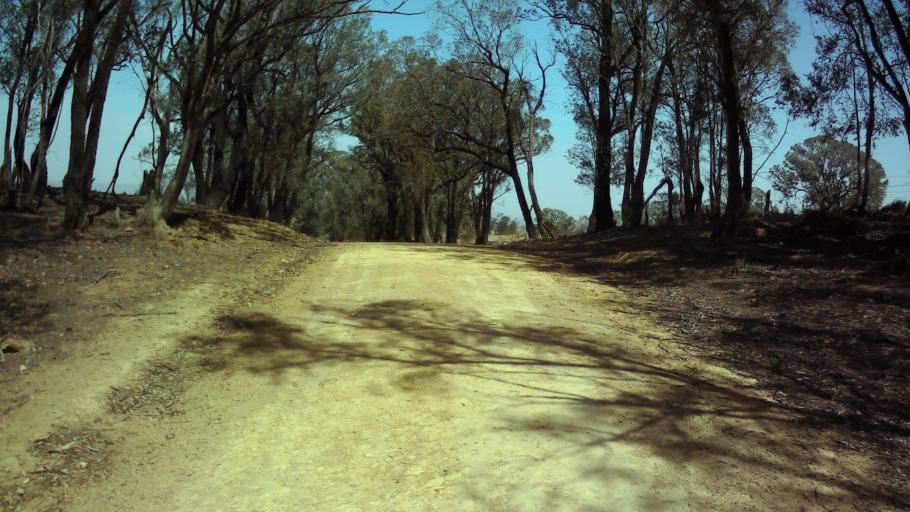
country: AU
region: New South Wales
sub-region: Weddin
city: Grenfell
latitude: -33.8979
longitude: 148.1304
